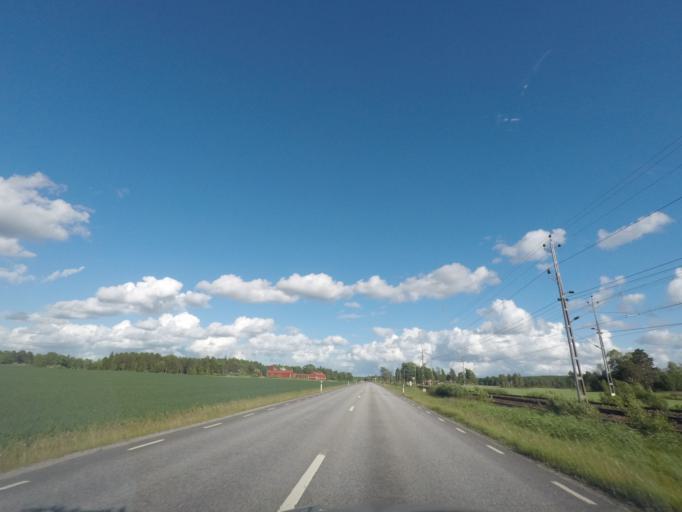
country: SE
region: Vaestmanland
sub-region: Arboga Kommun
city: Arboga
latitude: 59.4081
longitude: 15.7968
